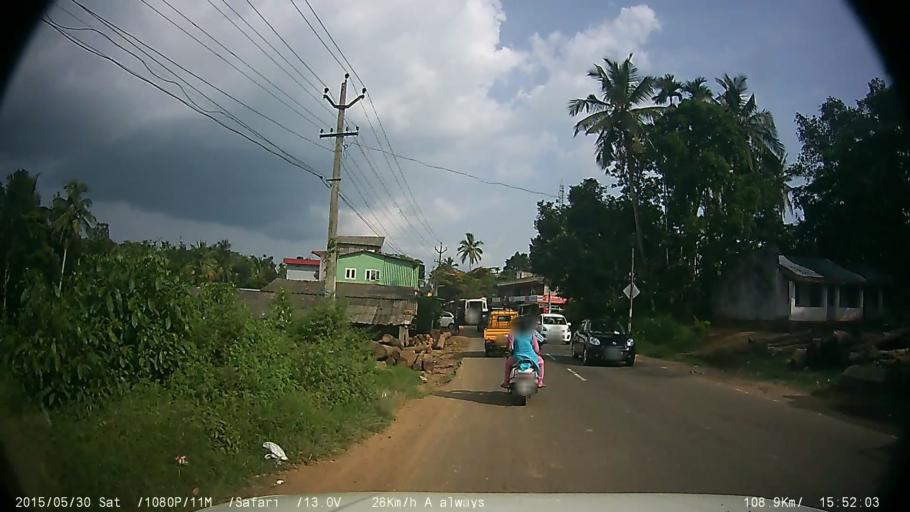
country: IN
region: Kerala
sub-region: Wayanad
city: Panamaram
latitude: 11.6782
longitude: 76.0745
